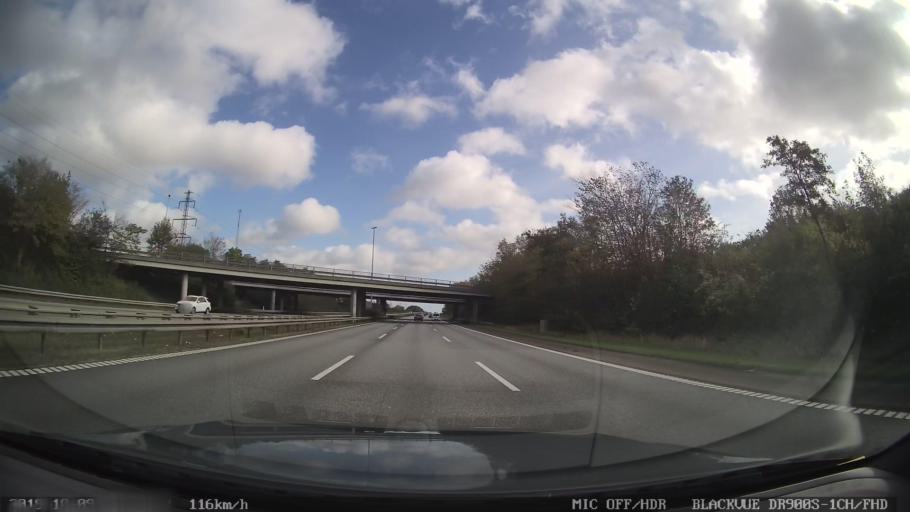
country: DK
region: Capital Region
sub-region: Vallensbaek Kommune
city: Vallensbaek
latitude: 55.6279
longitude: 12.3816
